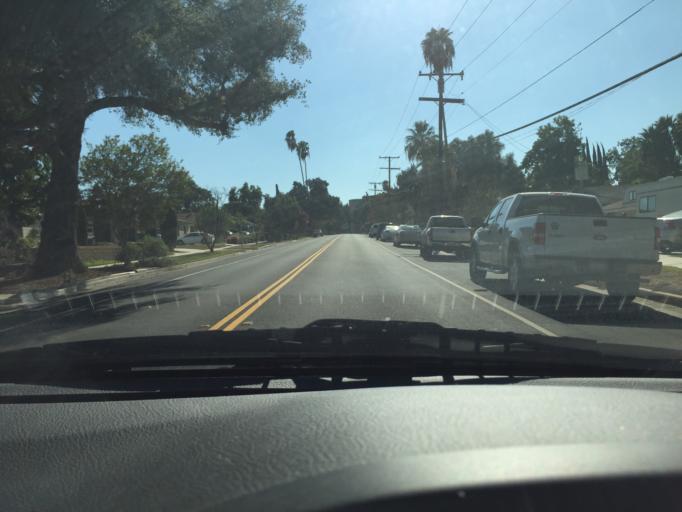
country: US
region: California
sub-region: San Bernardino County
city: Redlands
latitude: 34.0383
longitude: -117.2010
